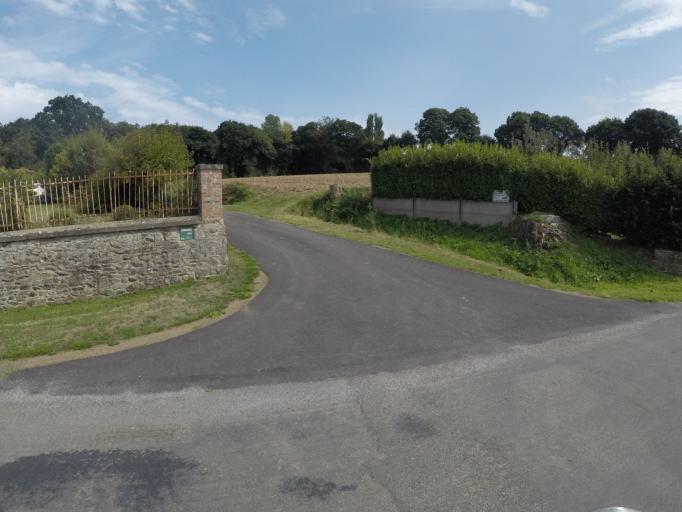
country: FR
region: Brittany
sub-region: Departement des Cotes-d'Armor
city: Goudelin
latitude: 48.6078
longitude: -3.0185
